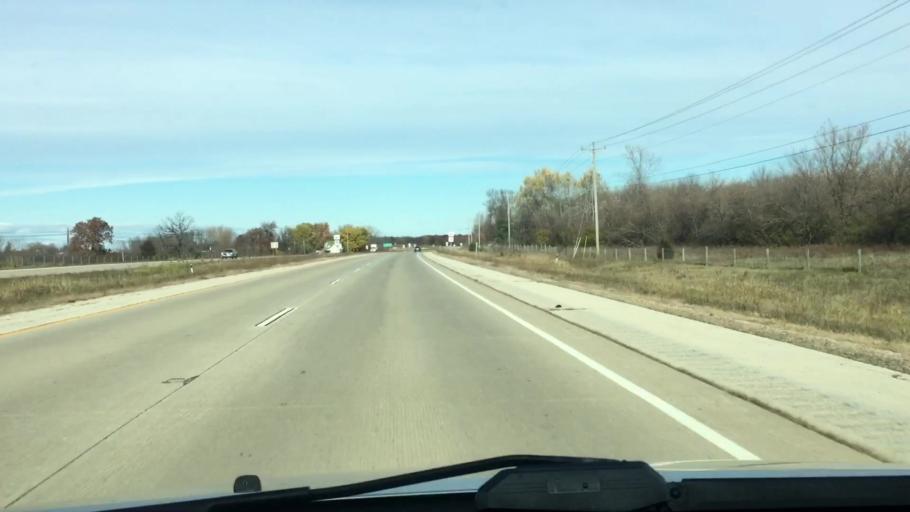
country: US
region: Wisconsin
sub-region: Brown County
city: Bellevue
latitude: 44.5781
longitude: -87.8731
